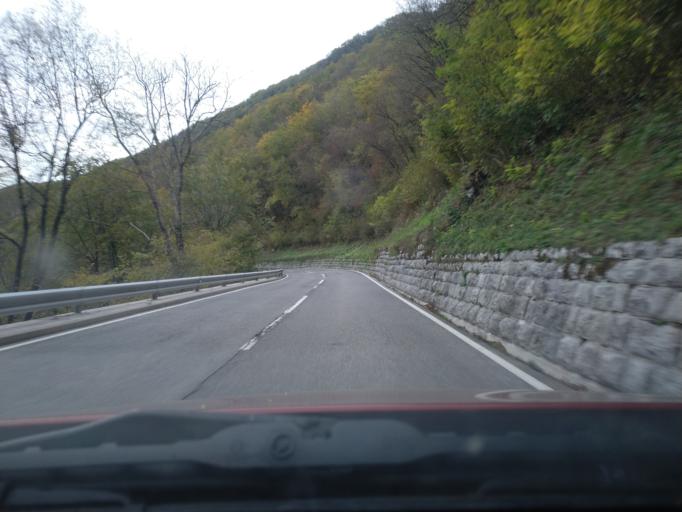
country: SI
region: Kobarid
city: Kobarid
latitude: 46.2724
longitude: 13.5705
